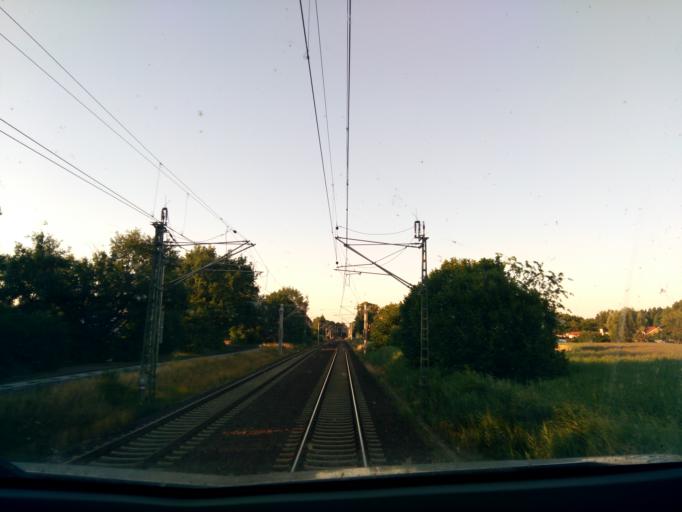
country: DE
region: Brandenburg
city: Bestensee
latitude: 52.2452
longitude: 13.6340
